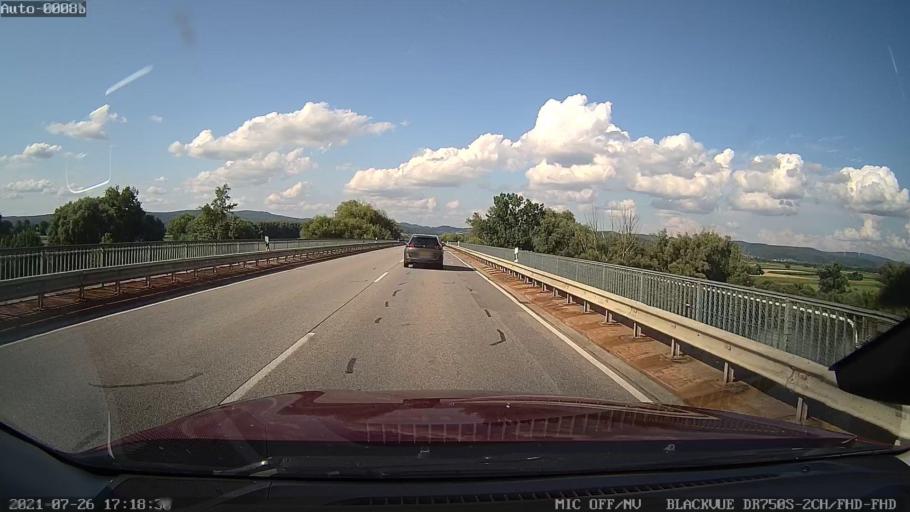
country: DE
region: Bavaria
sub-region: Upper Palatinate
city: Pfatter
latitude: 48.9755
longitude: 12.3569
